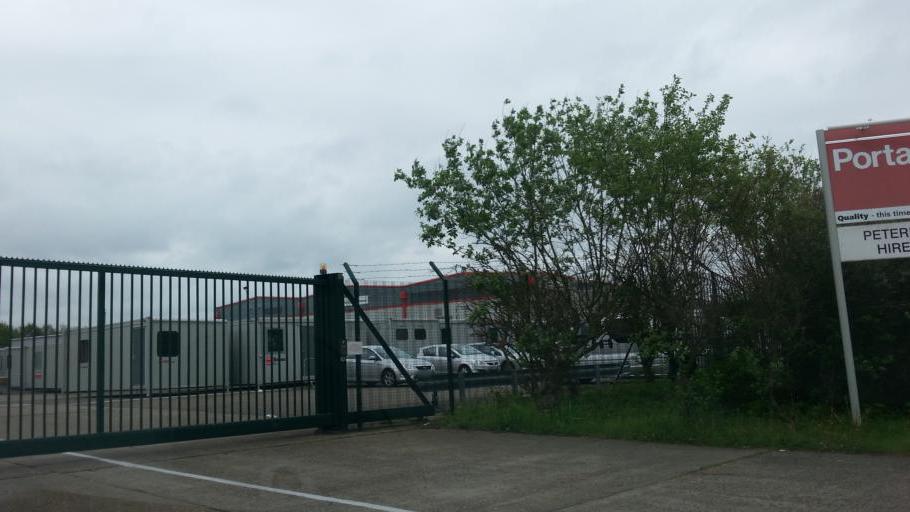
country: GB
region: England
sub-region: Peterborough
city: Marholm
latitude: 52.6164
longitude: -0.2898
